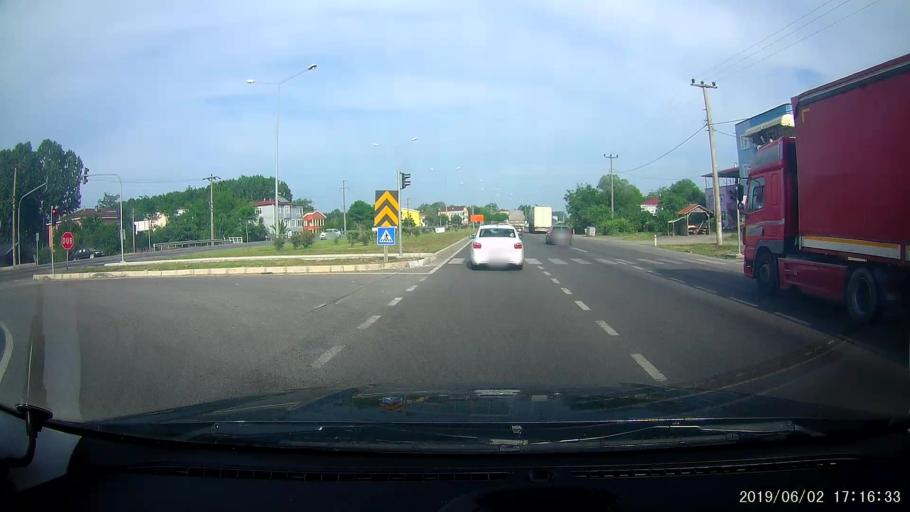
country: TR
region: Samsun
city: Dikbiyik
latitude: 41.2338
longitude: 36.5683
